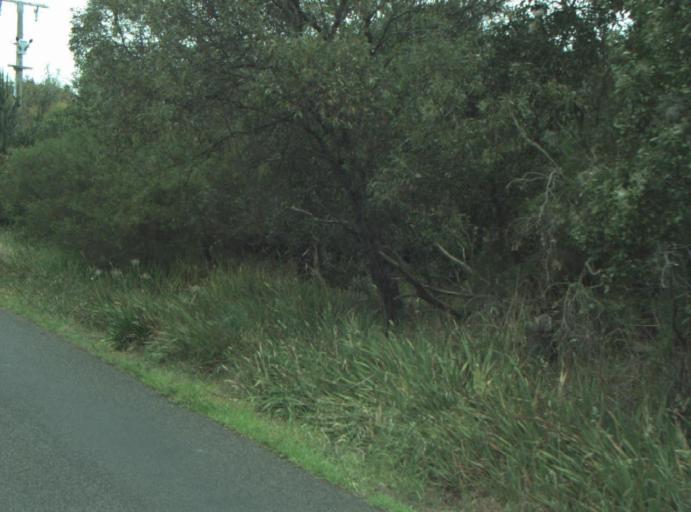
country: AU
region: Victoria
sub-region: Greater Geelong
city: Breakwater
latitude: -38.2016
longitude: 144.4109
